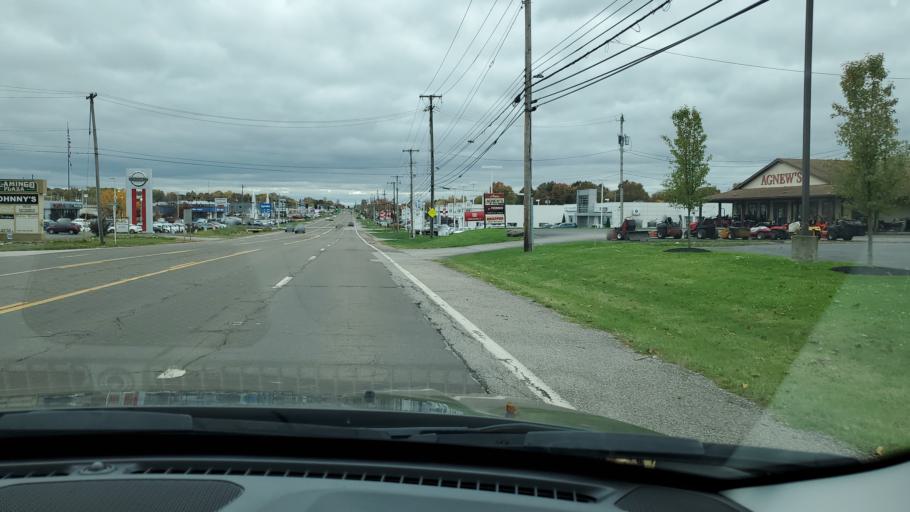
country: US
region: Ohio
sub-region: Mahoning County
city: Boardman
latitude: 41.0124
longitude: -80.6628
